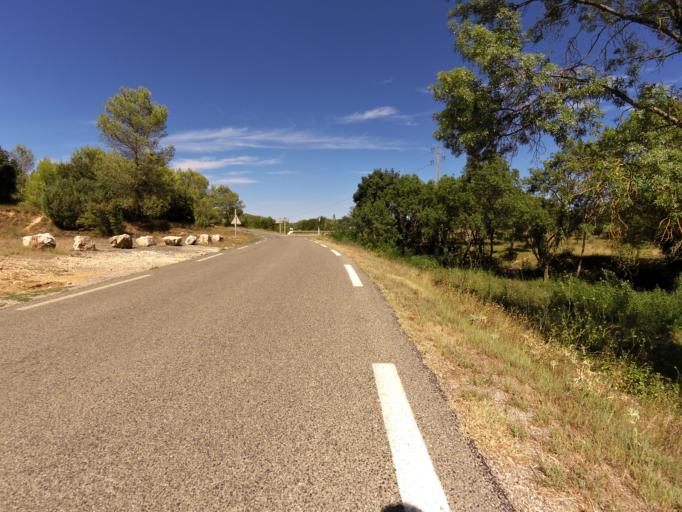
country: FR
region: Languedoc-Roussillon
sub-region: Departement du Gard
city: Quissac
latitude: 43.8849
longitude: 4.0478
